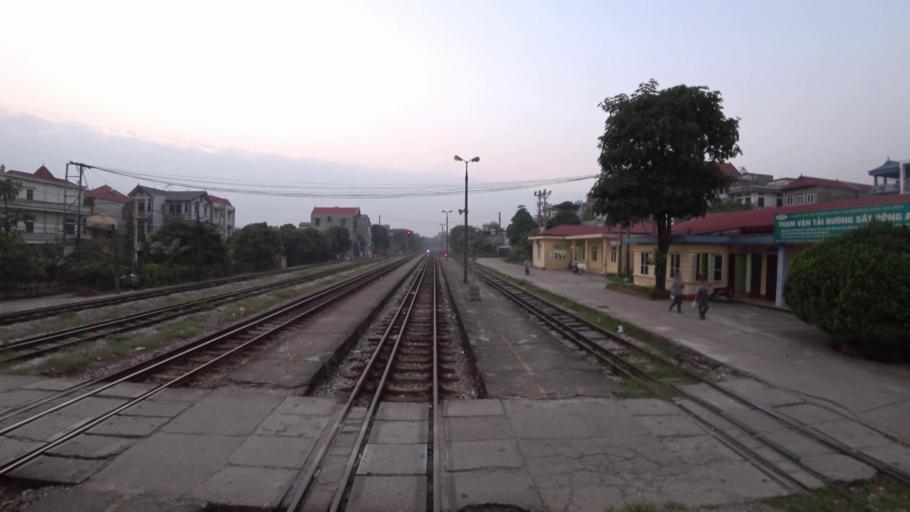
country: VN
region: Ha Noi
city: Soc Son
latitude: 21.2196
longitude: 105.8596
